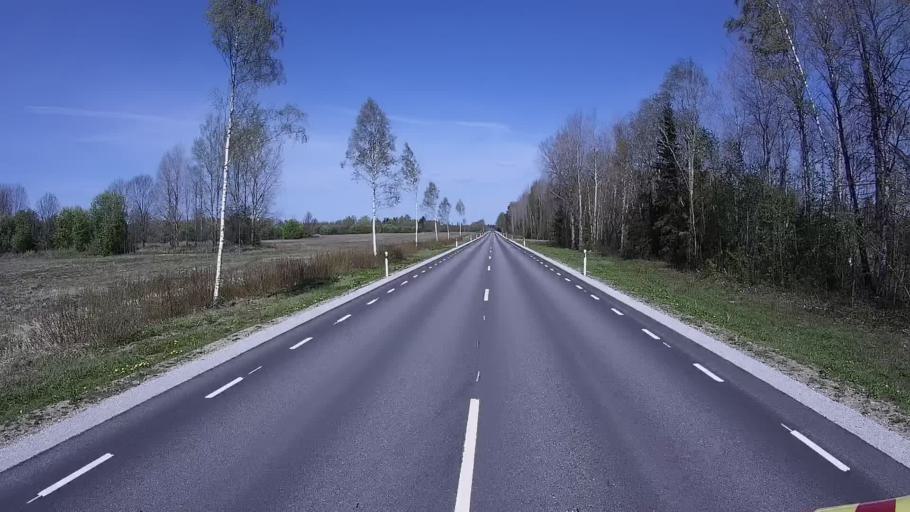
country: EE
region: Harju
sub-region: Nissi vald
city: Turba
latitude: 59.1595
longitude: 24.0741
